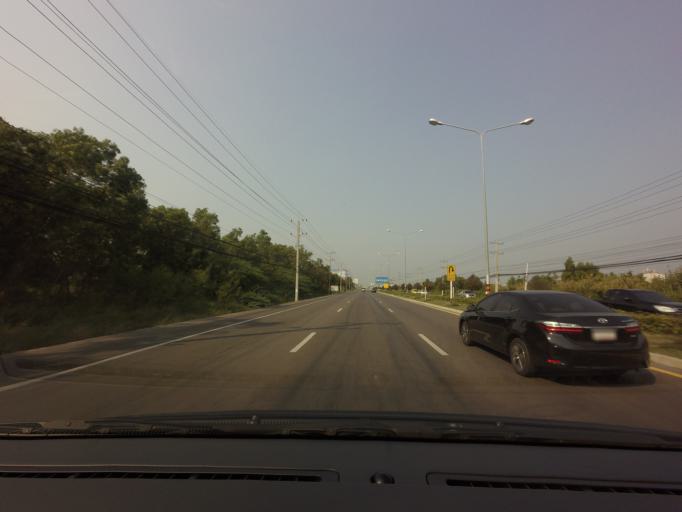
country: TH
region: Phetchaburi
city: Cha-am
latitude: 12.7663
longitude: 99.9646
